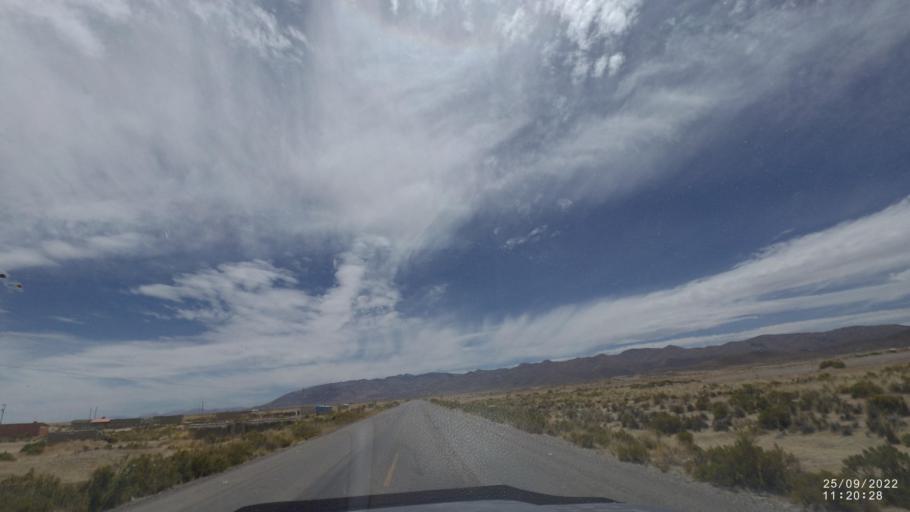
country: BO
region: Oruro
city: Challapata
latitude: -19.1586
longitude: -66.7759
